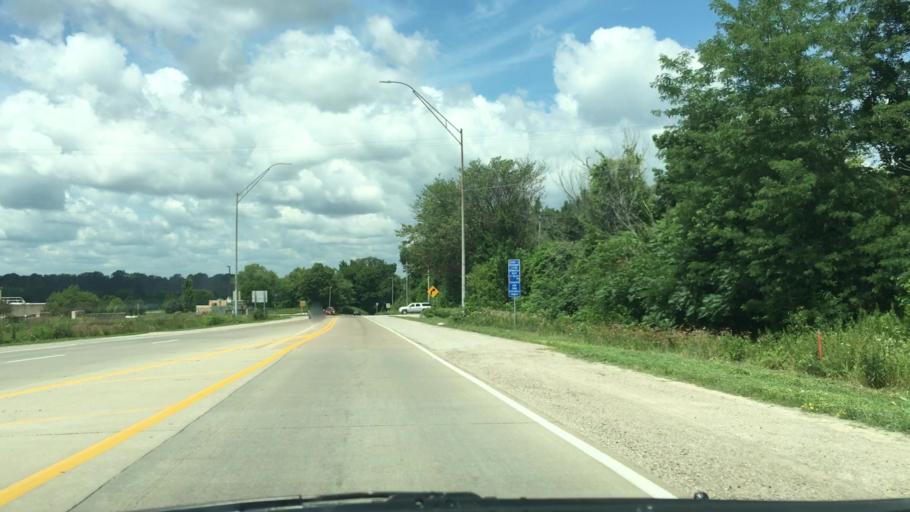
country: US
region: Iowa
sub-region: Johnson County
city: Iowa City
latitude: 41.6889
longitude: -91.5427
